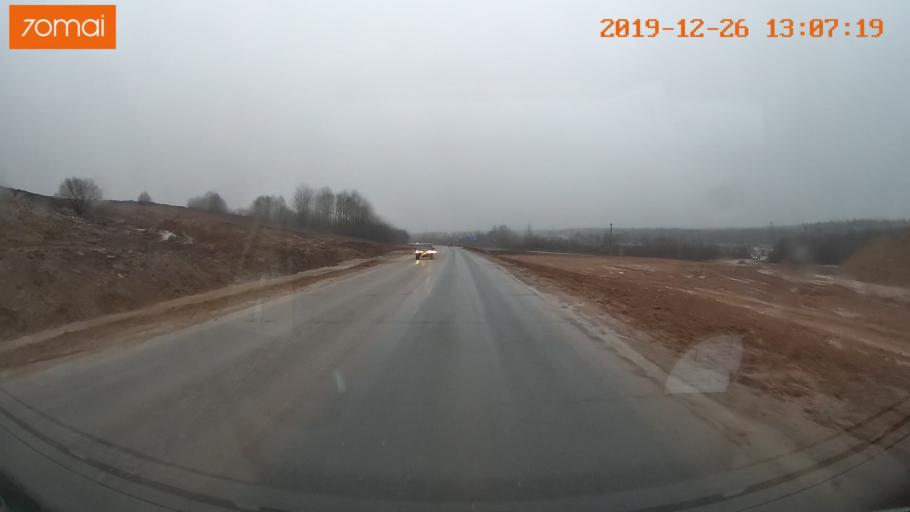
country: RU
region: Vologda
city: Cherepovets
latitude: 59.0674
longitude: 37.9164
